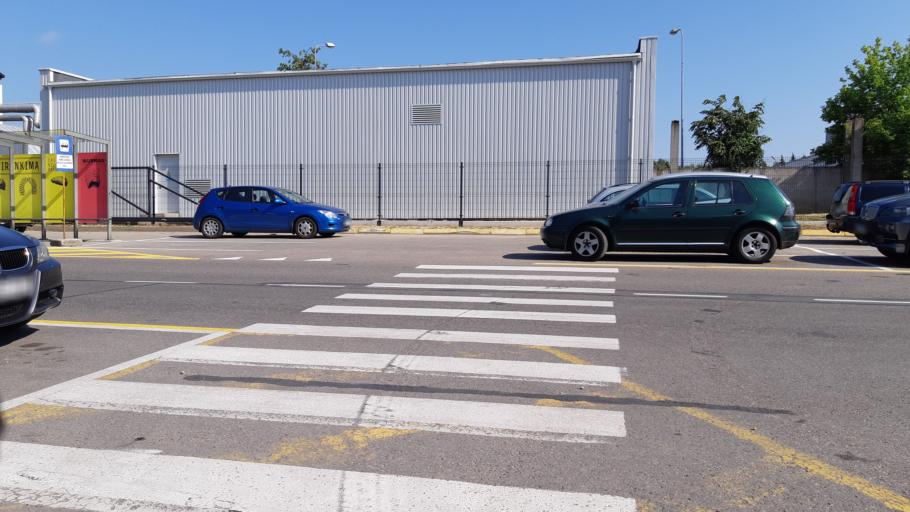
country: LT
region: Kauno apskritis
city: Dainava (Kaunas)
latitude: 54.9166
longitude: 23.9922
